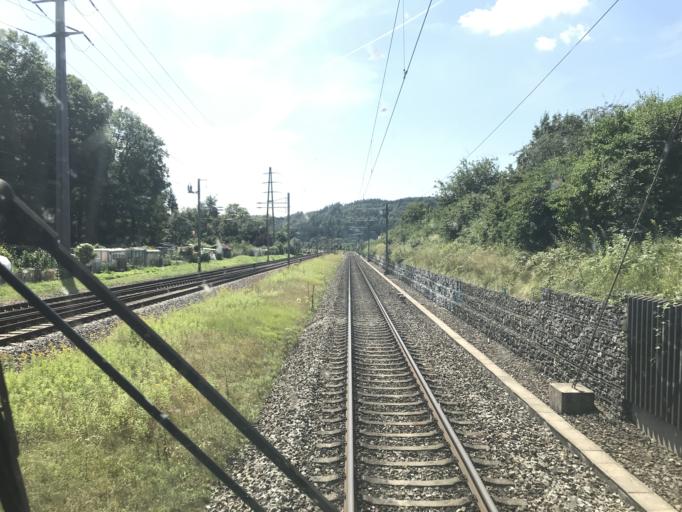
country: CH
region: Zurich
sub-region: Bezirk Winterthur
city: Toess (Kreis 4) / Eichliacker
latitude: 47.4835
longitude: 8.7099
